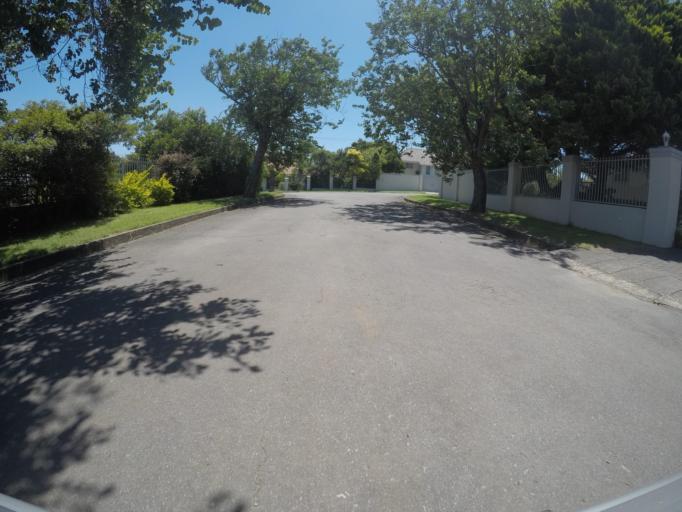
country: ZA
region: Eastern Cape
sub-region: Buffalo City Metropolitan Municipality
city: East London
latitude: -32.9861
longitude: 27.8972
